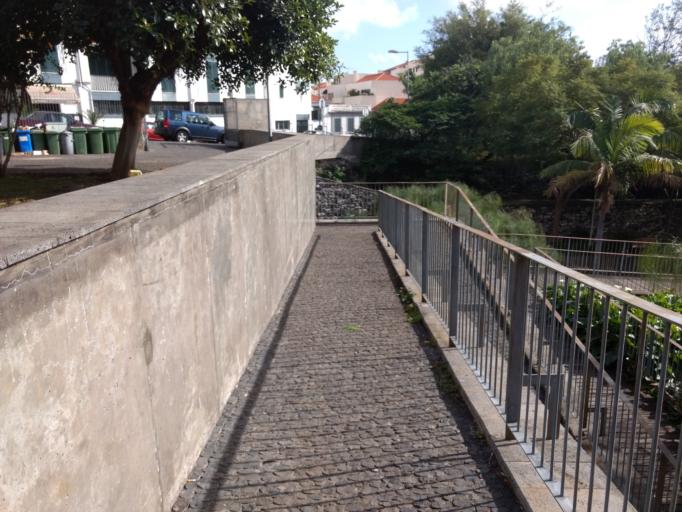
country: PT
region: Madeira
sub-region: Funchal
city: Nossa Senhora do Monte
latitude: 32.6539
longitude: -16.9115
